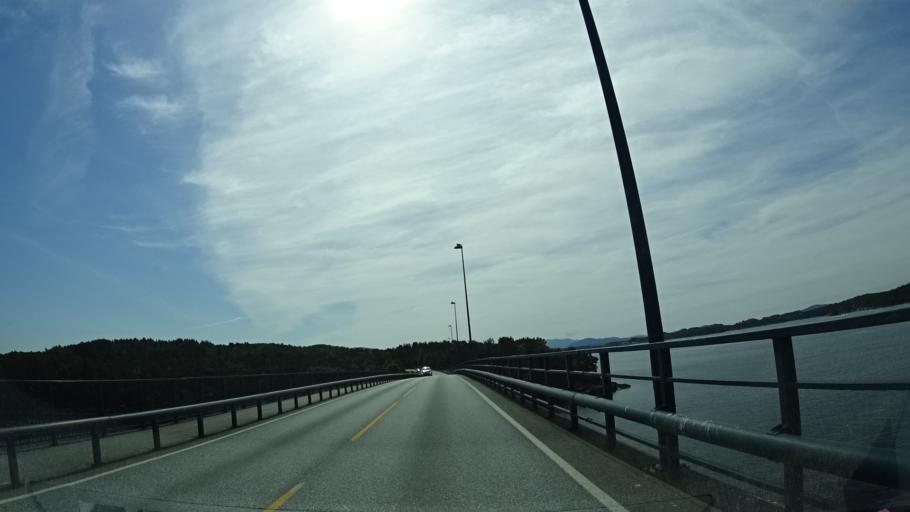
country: NO
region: Hordaland
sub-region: Bomlo
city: Mosterhamn
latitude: 59.7341
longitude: 5.3504
